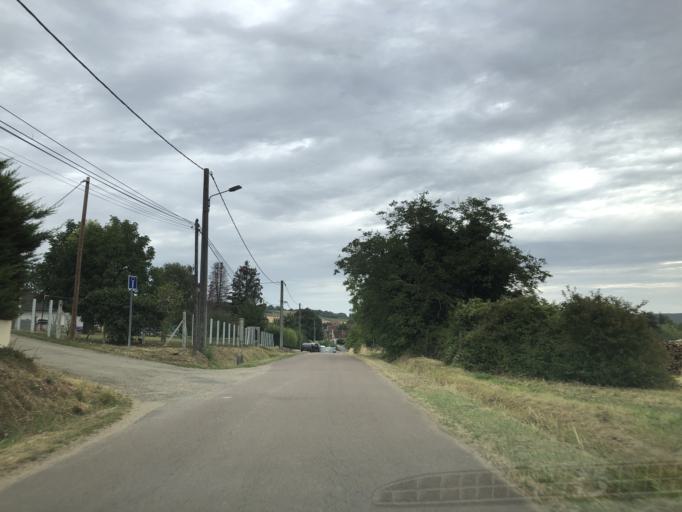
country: FR
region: Bourgogne
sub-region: Departement de l'Yonne
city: Aillant-sur-Tholon
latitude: 47.9152
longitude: 3.3242
